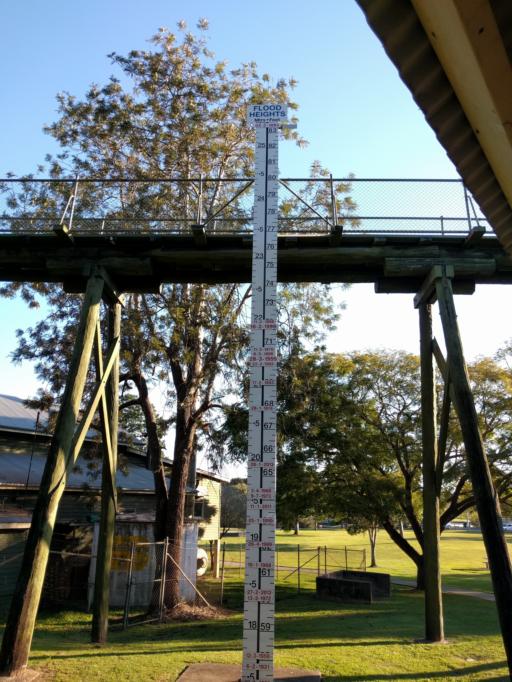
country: AU
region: Queensland
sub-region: Gympie Regional Council
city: Monkland
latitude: -26.2142
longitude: 152.6856
